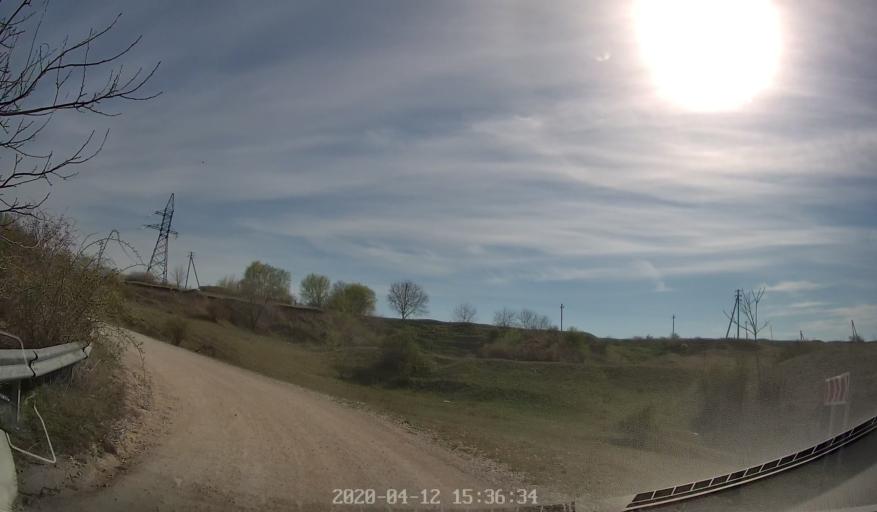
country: MD
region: Telenesti
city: Cocieri
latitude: 47.3247
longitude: 29.0670
